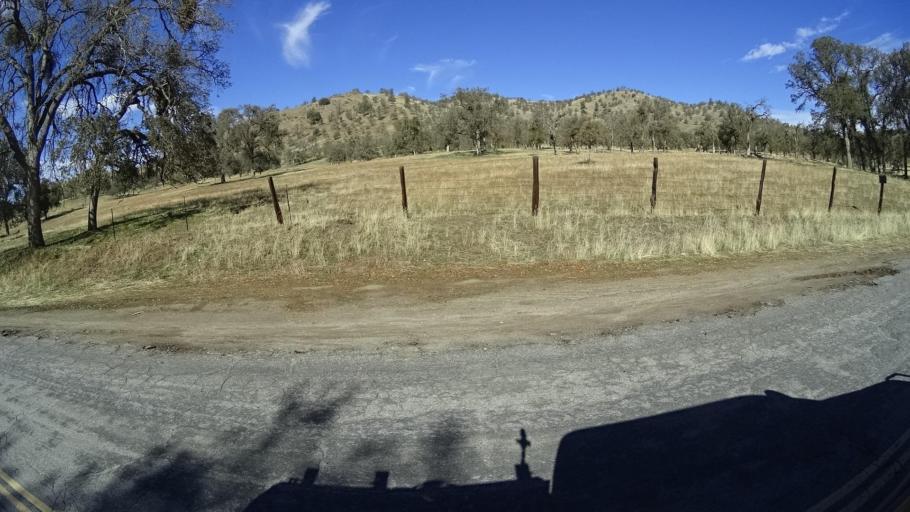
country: US
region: California
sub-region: Kern County
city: Alta Sierra
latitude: 35.6301
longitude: -118.7832
